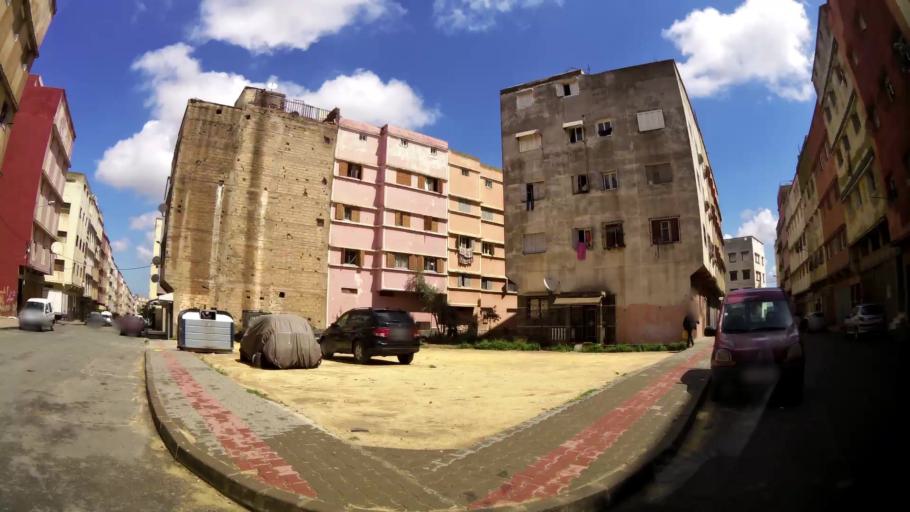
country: MA
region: Grand Casablanca
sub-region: Casablanca
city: Casablanca
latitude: 33.5363
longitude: -7.5673
